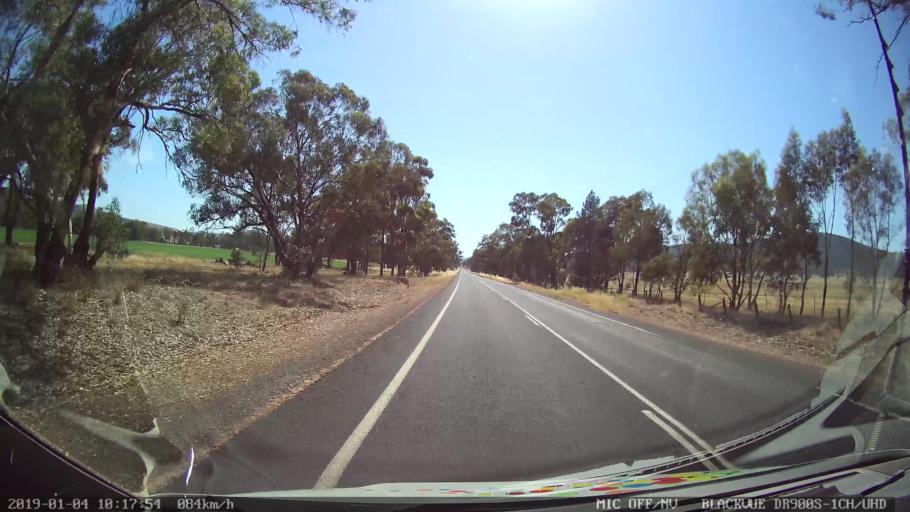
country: AU
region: New South Wales
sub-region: Cabonne
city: Canowindra
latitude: -33.3835
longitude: 148.4584
